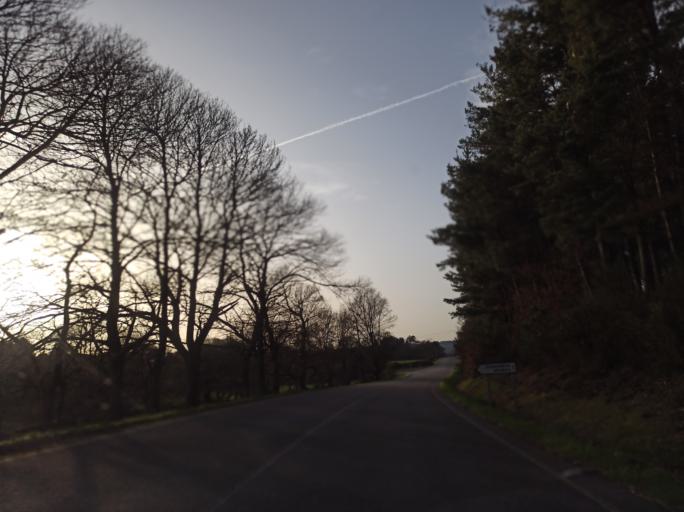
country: ES
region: Galicia
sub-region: Provincia de Lugo
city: Friol
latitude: 43.0216
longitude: -7.8266
